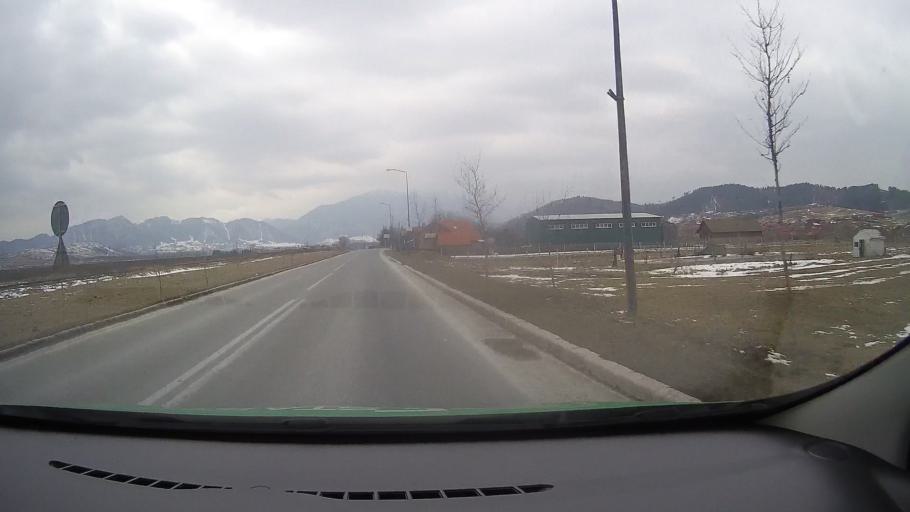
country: RO
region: Brasov
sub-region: Comuna Zarnesti
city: Tohanu Nou
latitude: 45.5778
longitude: 25.3829
